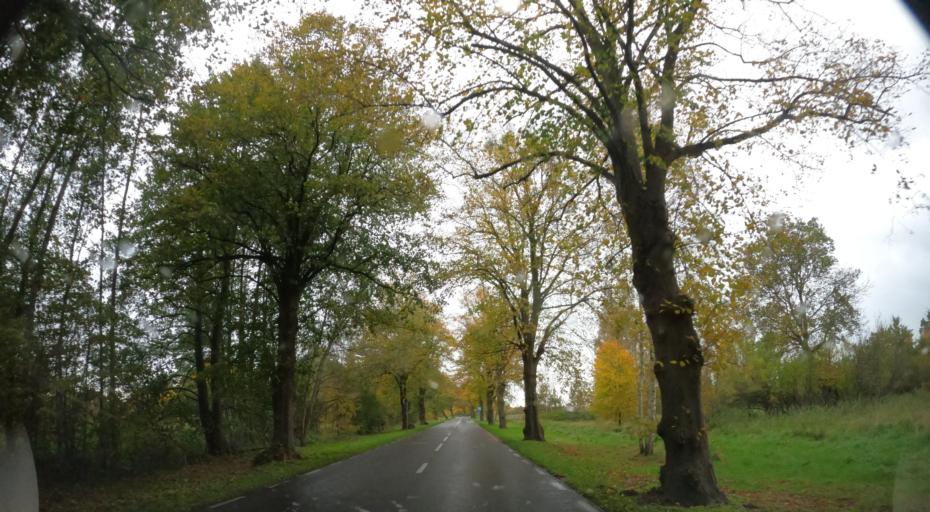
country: PL
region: West Pomeranian Voivodeship
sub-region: Powiat goleniowski
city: Goleniow
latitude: 53.5923
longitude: 14.7404
